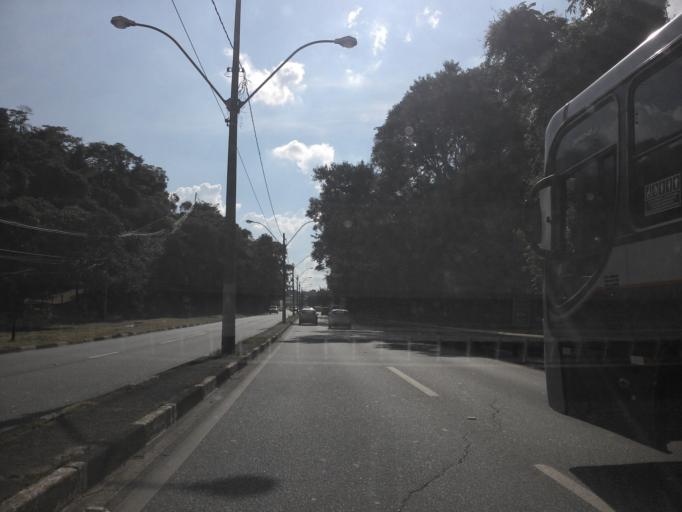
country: BR
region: Sao Paulo
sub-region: Valinhos
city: Valinhos
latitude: -22.9611
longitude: -47.0131
